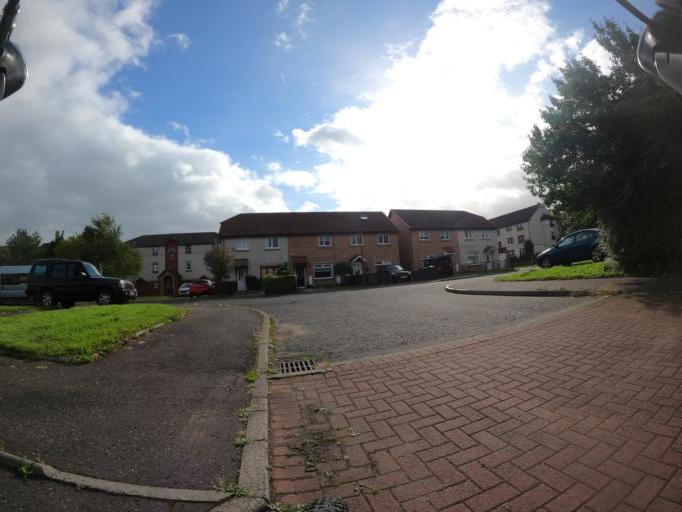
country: GB
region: Scotland
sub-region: Edinburgh
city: Colinton
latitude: 55.9702
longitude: -3.2593
